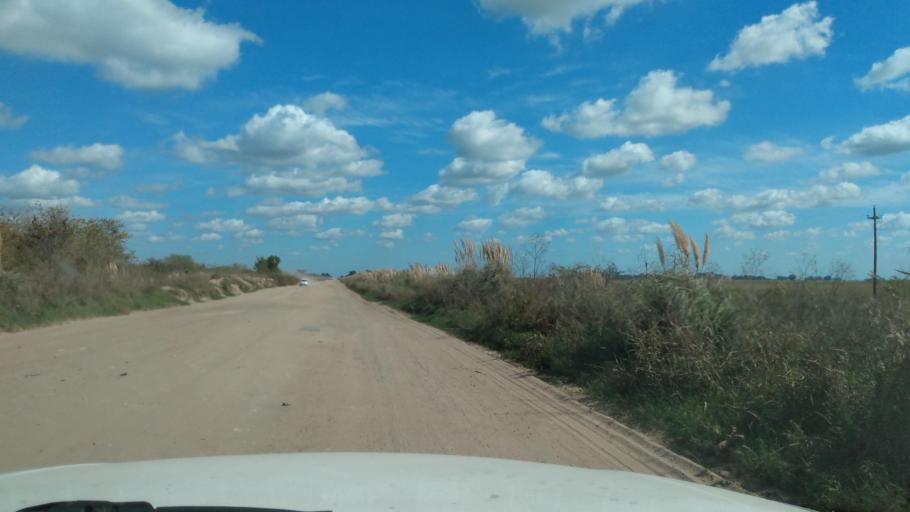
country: AR
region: Buenos Aires
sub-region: Partido de Navarro
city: Navarro
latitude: -35.0020
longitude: -59.3552
